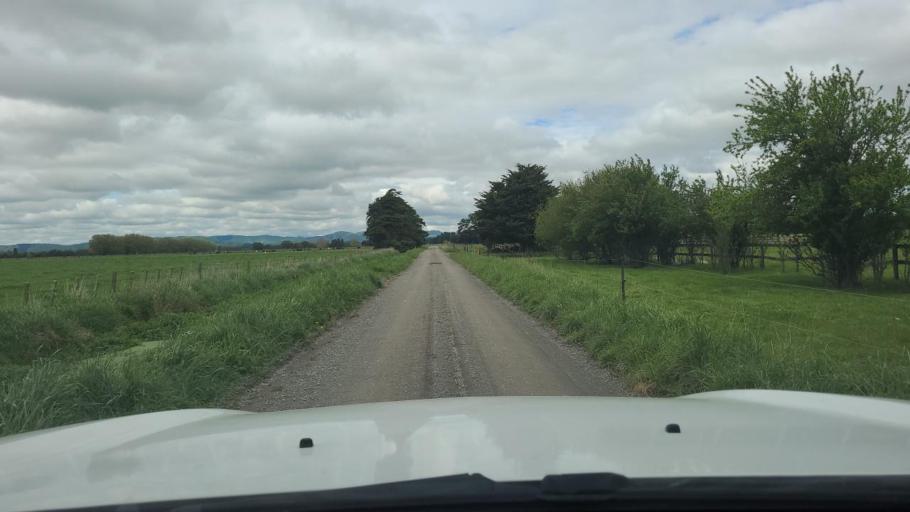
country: NZ
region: Wellington
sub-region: South Wairarapa District
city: Waipawa
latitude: -41.1474
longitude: 175.3851
